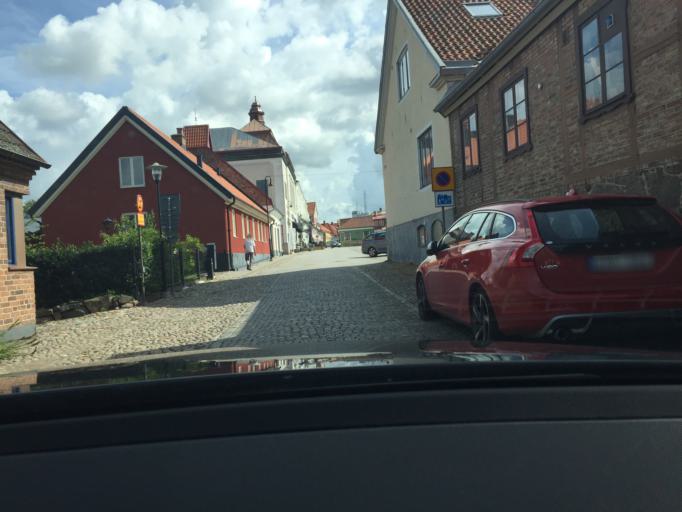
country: SE
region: Halland
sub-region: Laholms Kommun
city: Laholm
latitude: 56.5140
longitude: 13.0412
